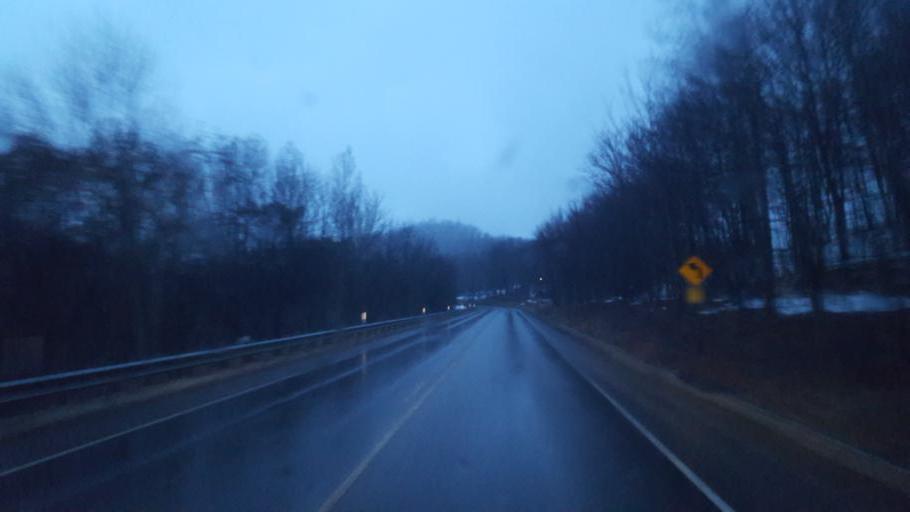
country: US
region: Pennsylvania
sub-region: McKean County
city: Smethport
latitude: 41.8241
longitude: -78.3787
